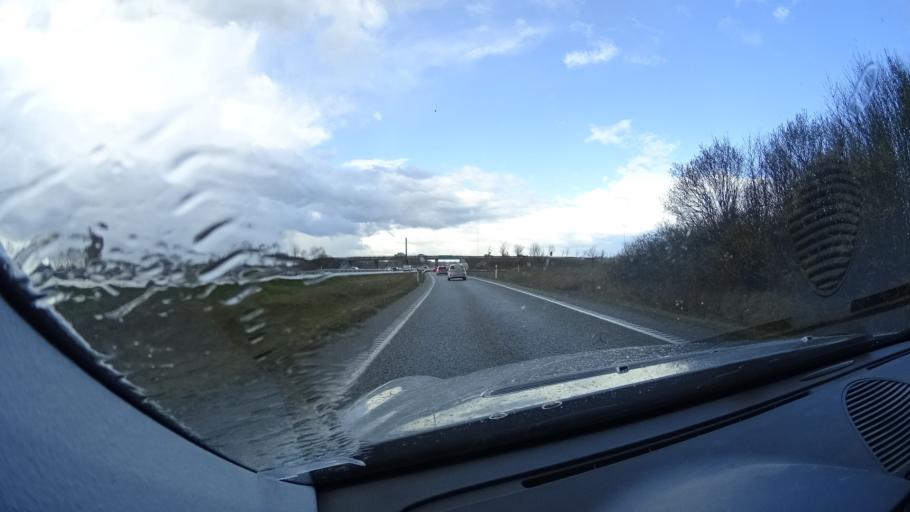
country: SE
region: Skane
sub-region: Lomma Kommun
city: Lomma
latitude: 55.6848
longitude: 13.0983
